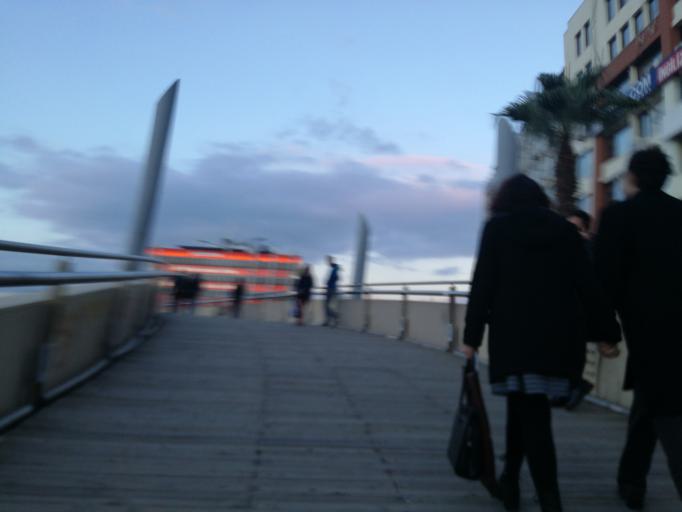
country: TR
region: Izmir
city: Izmir
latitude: 38.4216
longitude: 27.1304
